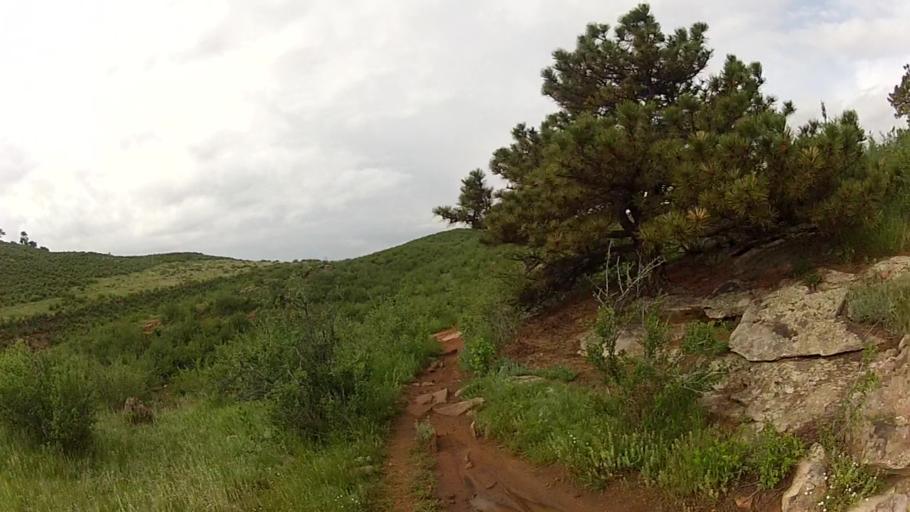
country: US
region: Colorado
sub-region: Larimer County
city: Loveland
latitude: 40.4436
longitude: -105.1539
